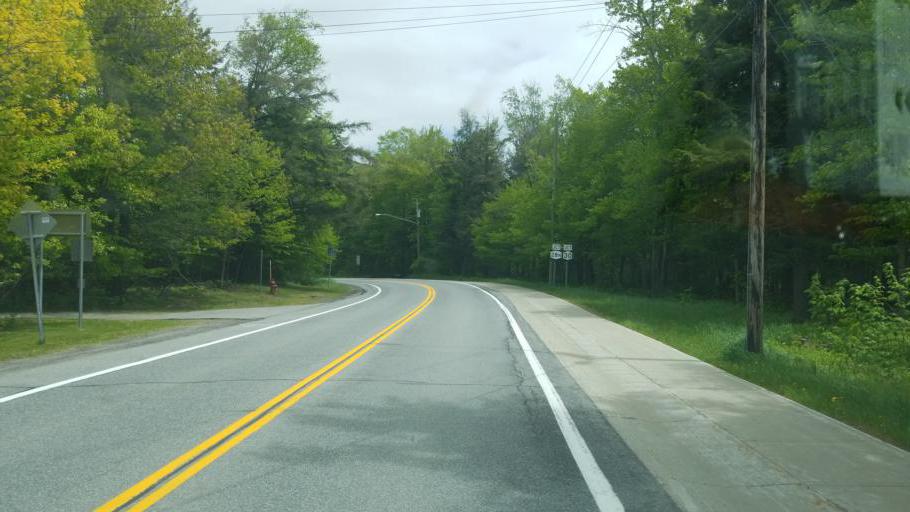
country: US
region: New York
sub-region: Franklin County
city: Tupper Lake
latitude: 43.8553
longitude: -74.4325
